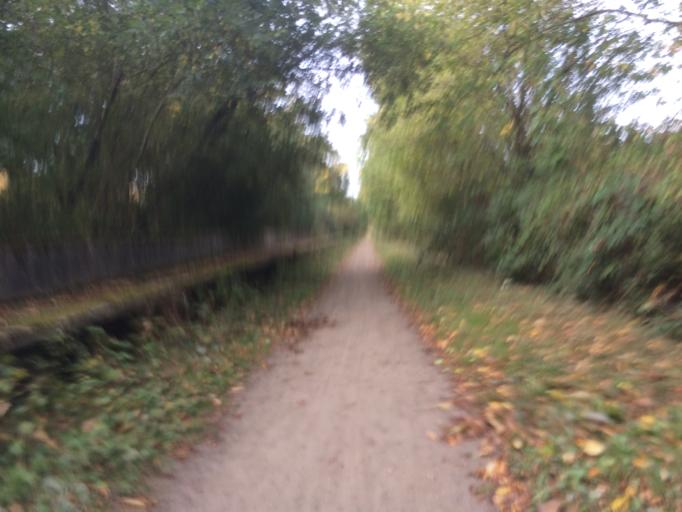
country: FR
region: Ile-de-France
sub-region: Departement de l'Essonne
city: Limours
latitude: 48.6568
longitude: 2.0832
